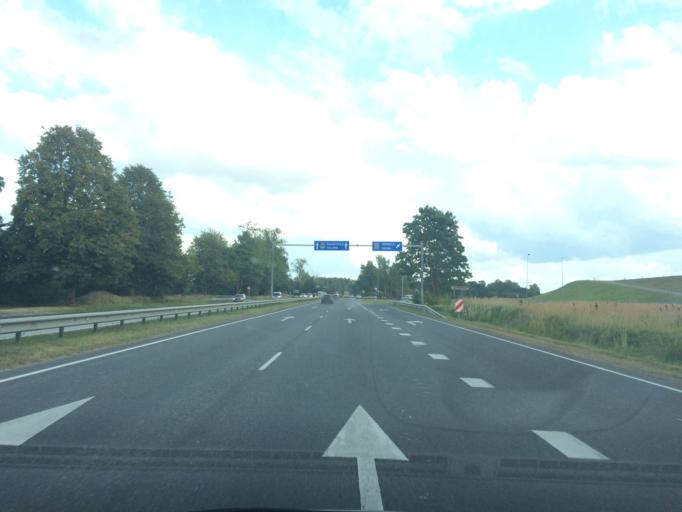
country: LV
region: Salaspils
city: Salaspils
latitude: 56.8585
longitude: 24.3119
